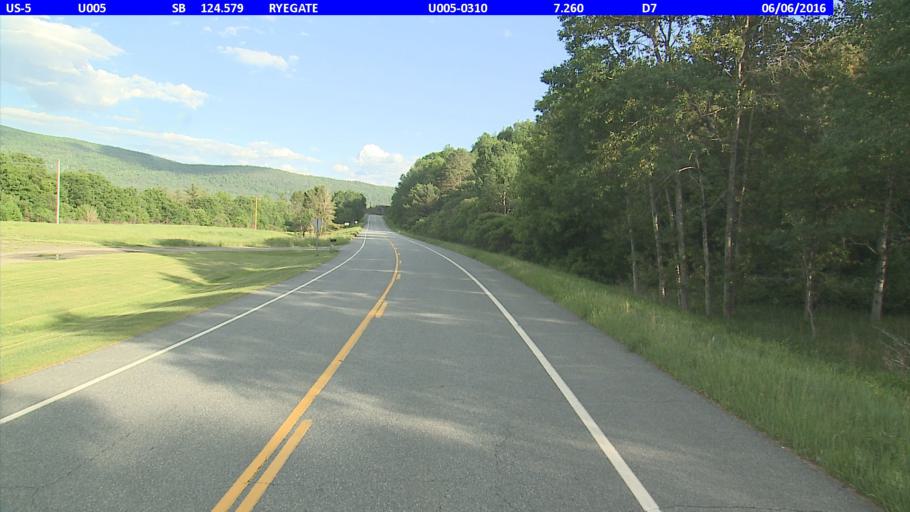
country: US
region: New Hampshire
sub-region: Grafton County
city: Woodsville
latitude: 44.2549
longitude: -72.0609
